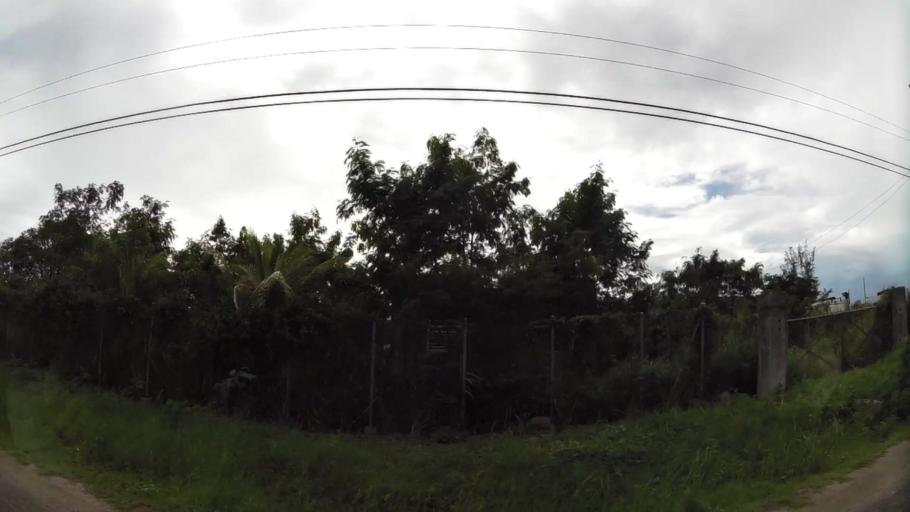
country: AG
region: Saint John
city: Potters Village
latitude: 17.0895
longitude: -61.8142
